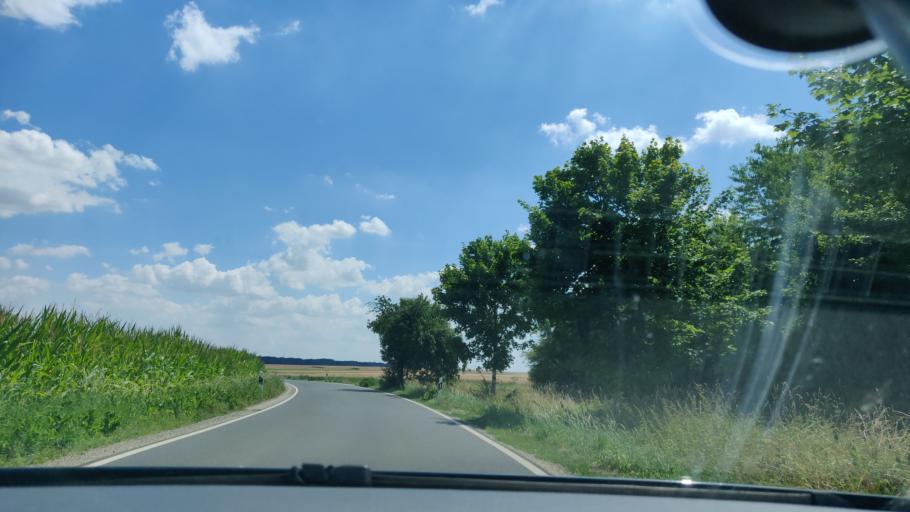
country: DE
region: Hesse
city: Gudensberg
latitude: 51.1544
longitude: 9.3609
